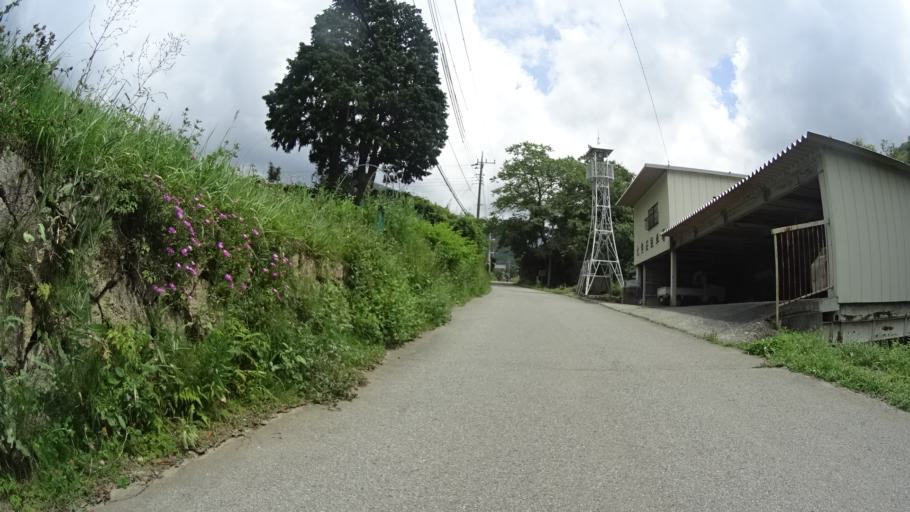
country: JP
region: Yamanashi
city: Nirasaki
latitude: 35.8951
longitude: 138.5393
